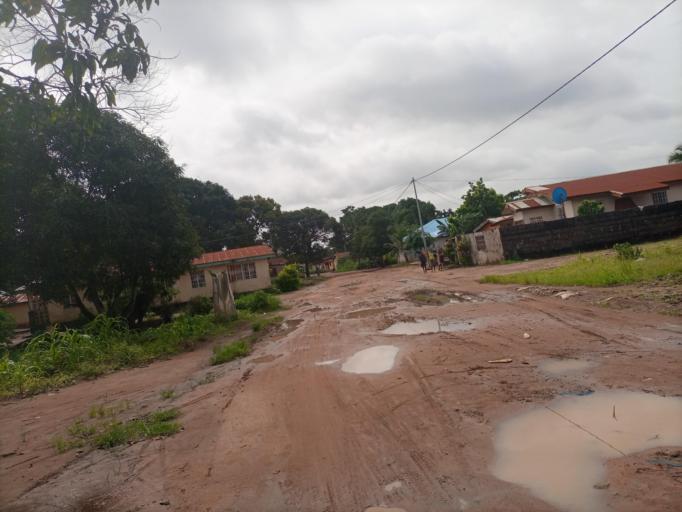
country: SL
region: Northern Province
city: Sawkta
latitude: 8.6245
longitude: -13.2055
